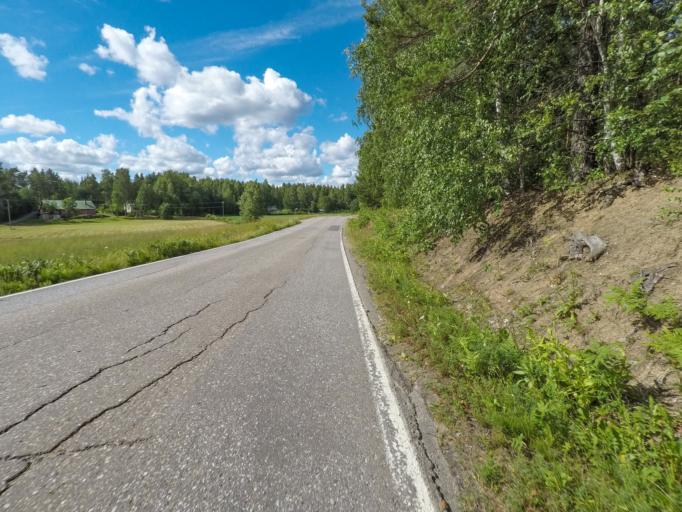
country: FI
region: South Karelia
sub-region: Lappeenranta
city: Joutseno
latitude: 61.1094
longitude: 28.3699
